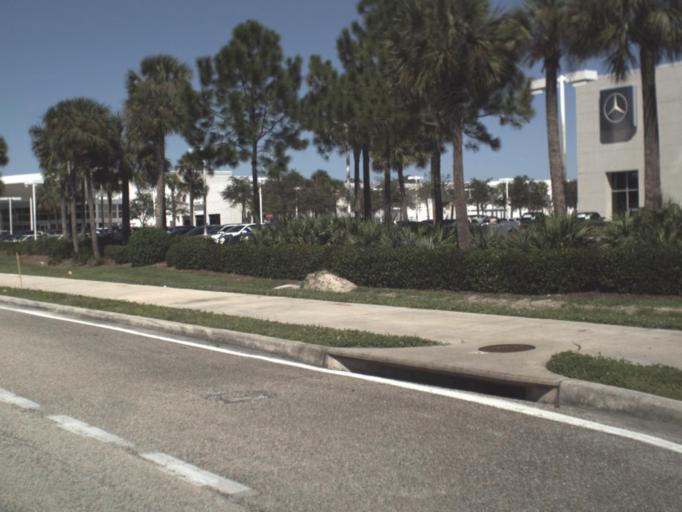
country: US
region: Florida
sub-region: Lee County
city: Villas
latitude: 26.5182
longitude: -81.8669
